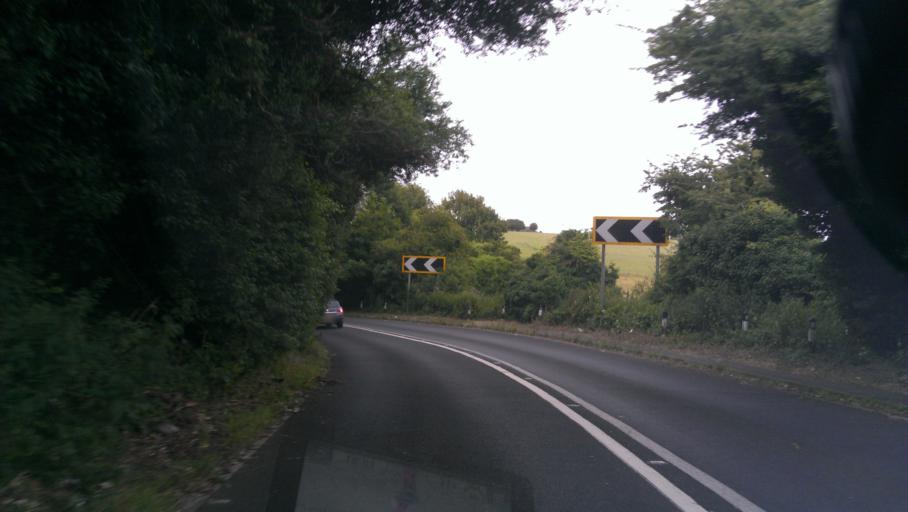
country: GB
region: England
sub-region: Kent
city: Dover
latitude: 51.1385
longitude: 1.3269
